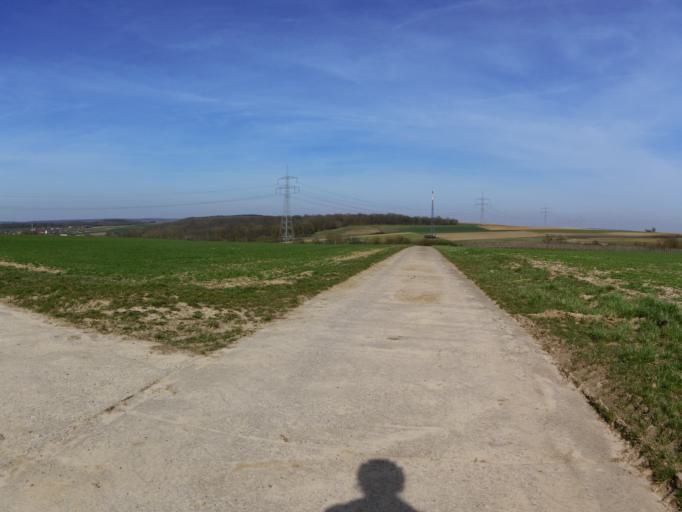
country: DE
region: Bavaria
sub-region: Regierungsbezirk Unterfranken
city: Biebelried
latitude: 49.8003
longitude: 10.0726
